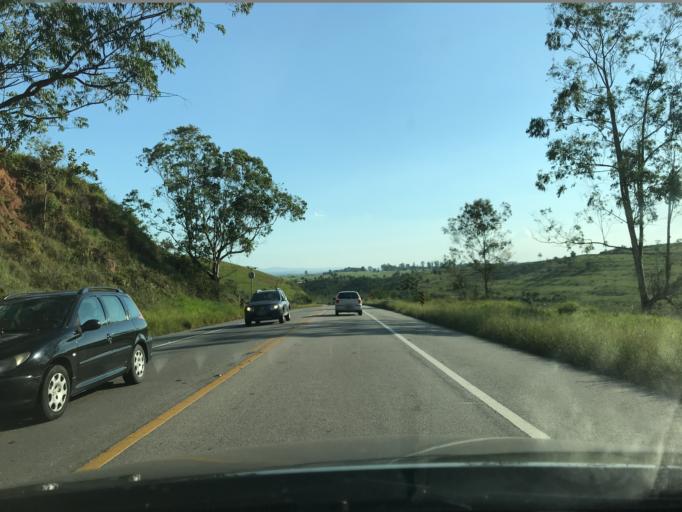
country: BR
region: Sao Paulo
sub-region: Tremembe
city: Tremembe
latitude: -22.9186
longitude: -45.5927
